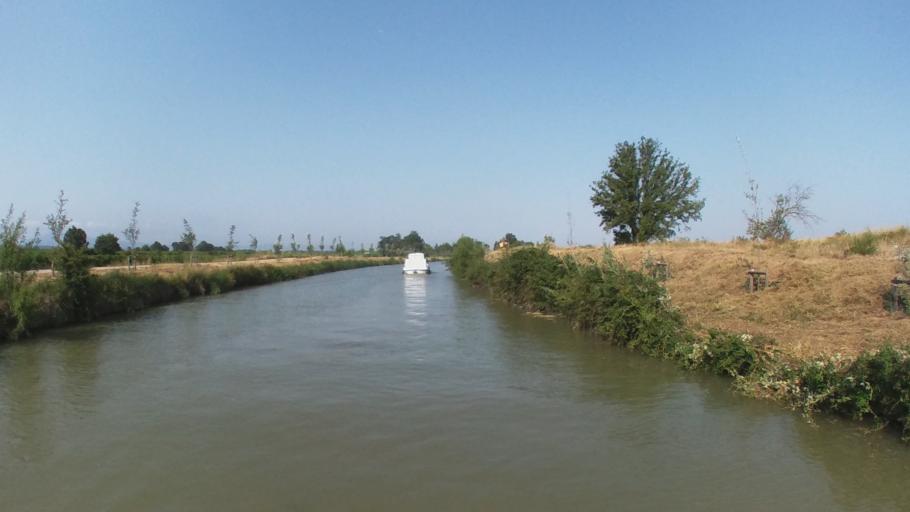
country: FR
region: Languedoc-Roussillon
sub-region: Departement de l'Aude
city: Pepieux
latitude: 43.2637
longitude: 2.6949
